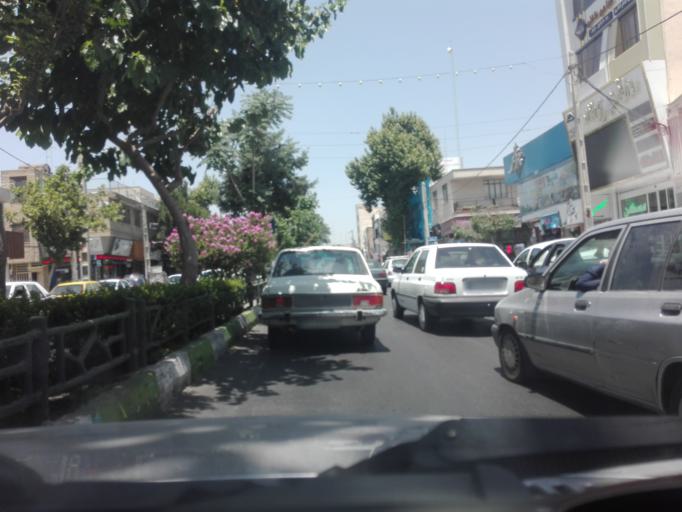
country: IR
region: Tehran
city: Shahre Jadide Andisheh
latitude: 35.7179
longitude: 50.9866
